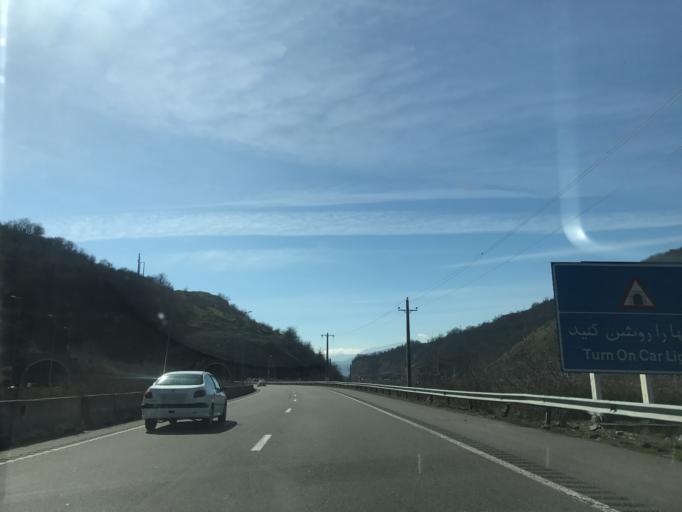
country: IR
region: Gilan
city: Pa'in-e Bazar-e Rudbar
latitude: 36.9536
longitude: 49.5507
